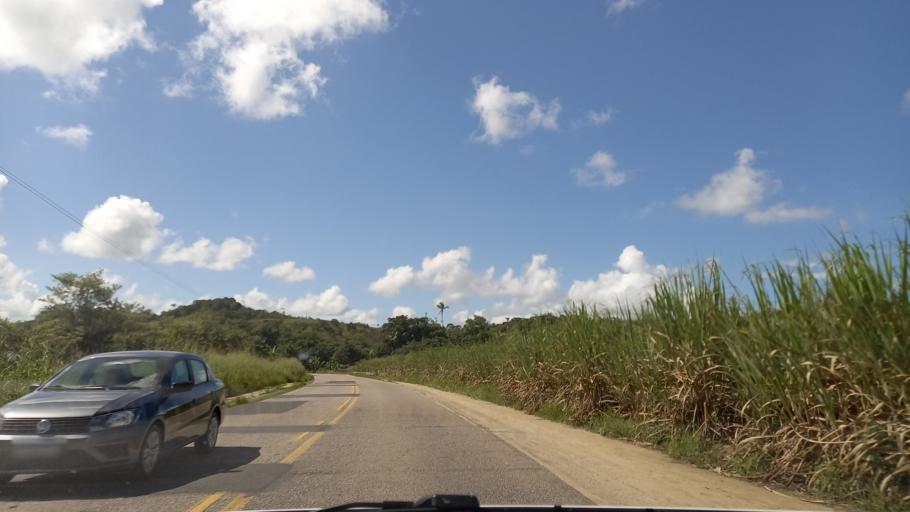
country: BR
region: Pernambuco
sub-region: Barreiros
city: Barreiros
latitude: -8.7764
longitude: -35.1736
